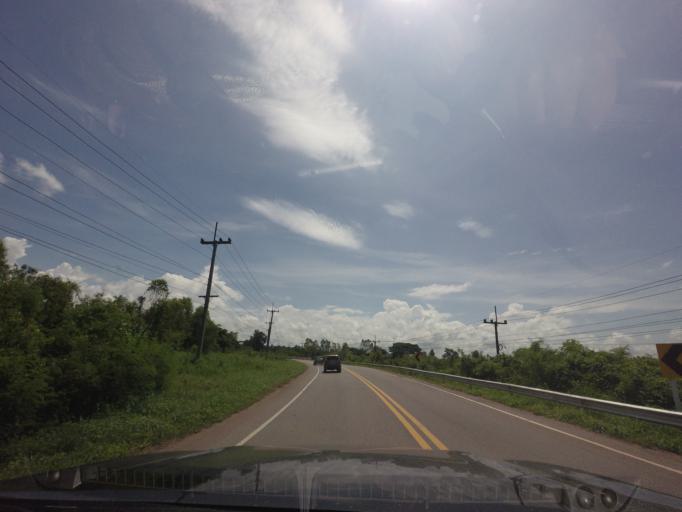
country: TH
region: Changwat Udon Thani
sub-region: Amphoe Ban Phue
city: Ban Phue
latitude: 17.7138
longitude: 102.4123
